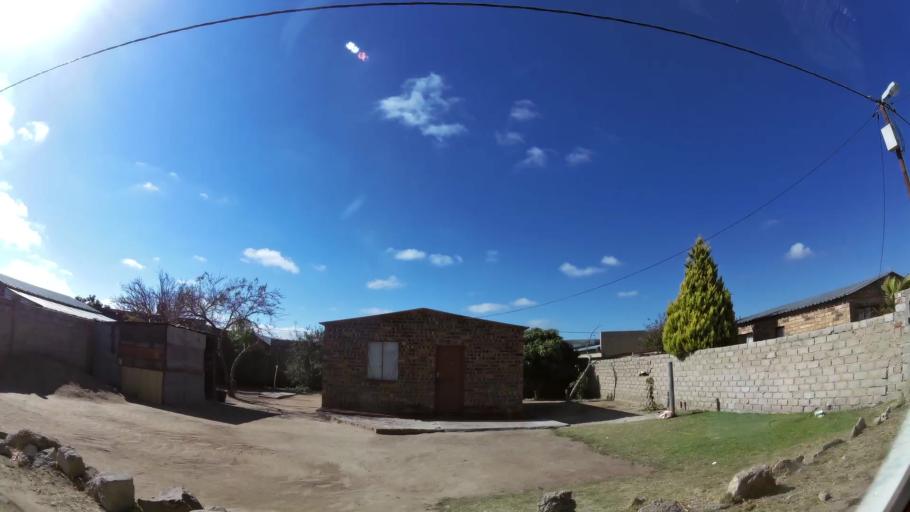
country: ZA
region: Limpopo
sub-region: Capricorn District Municipality
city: Polokwane
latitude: -23.8597
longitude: 29.3982
